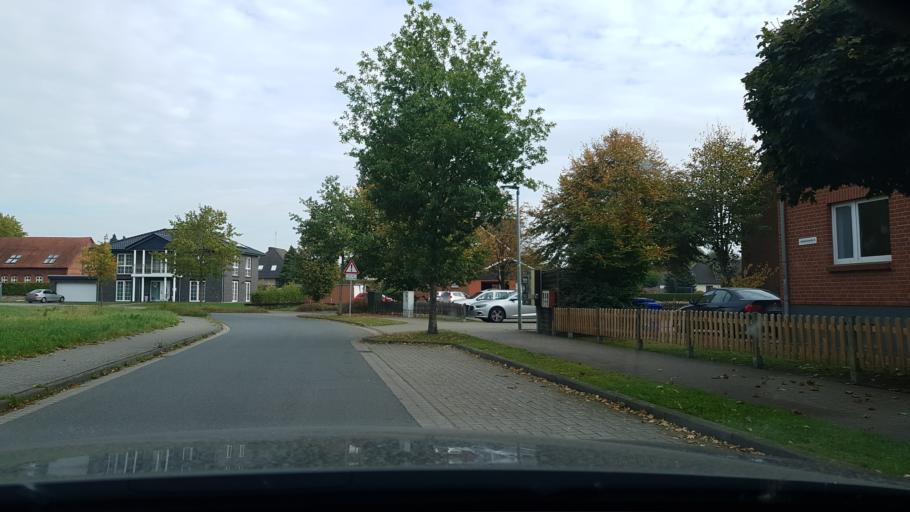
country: DE
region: Lower Saxony
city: Beverstedt
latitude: 53.4302
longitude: 8.8144
